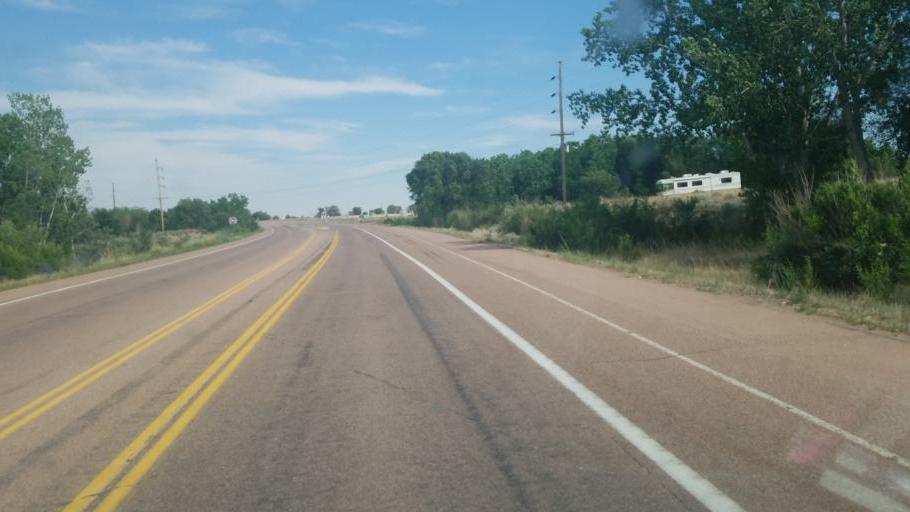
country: US
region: Colorado
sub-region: Pueblo County
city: Pueblo
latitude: 38.2360
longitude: -104.3301
